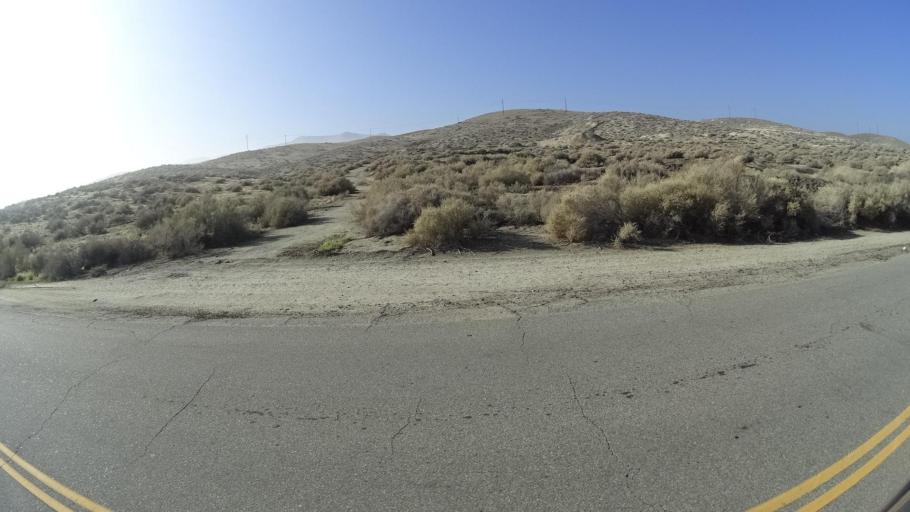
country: US
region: California
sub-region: Kern County
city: Taft Heights
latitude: 35.1903
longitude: -119.5735
